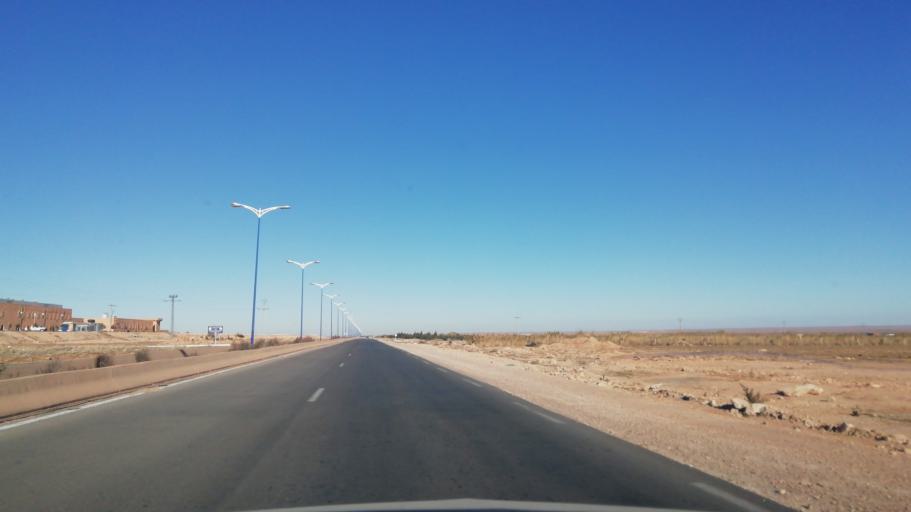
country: DZ
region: Wilaya de Naama
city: Naama
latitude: 33.5454
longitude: -0.2489
